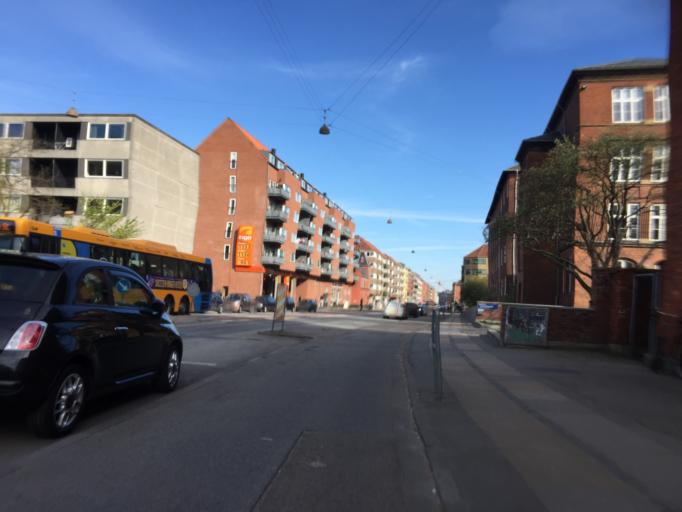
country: DK
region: Capital Region
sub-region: Frederiksberg Kommune
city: Frederiksberg
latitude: 55.7053
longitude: 12.5244
